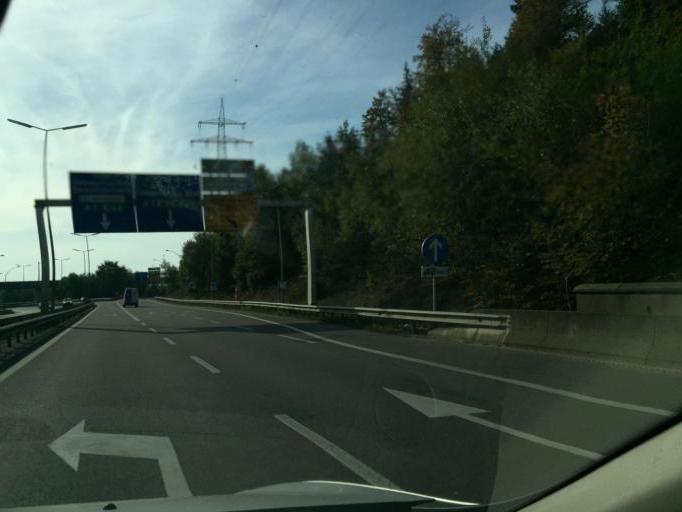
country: LU
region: Luxembourg
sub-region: Canton de Luxembourg
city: Sandweiler
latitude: 49.6436
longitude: 6.1883
